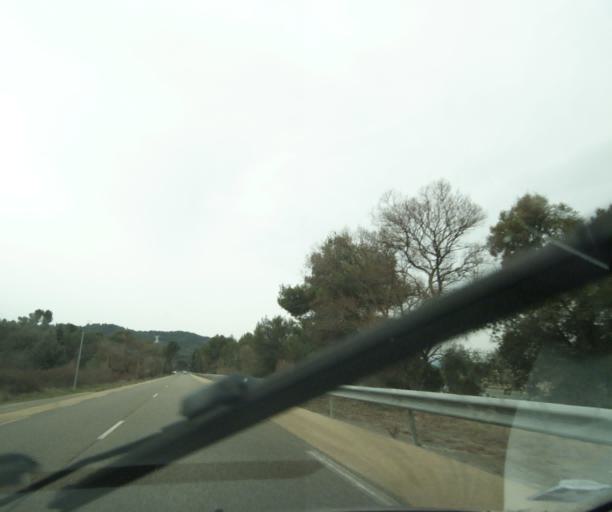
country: FR
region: Provence-Alpes-Cote d'Azur
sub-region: Departement des Bouches-du-Rhone
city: Jouques
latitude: 43.6737
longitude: 5.6504
